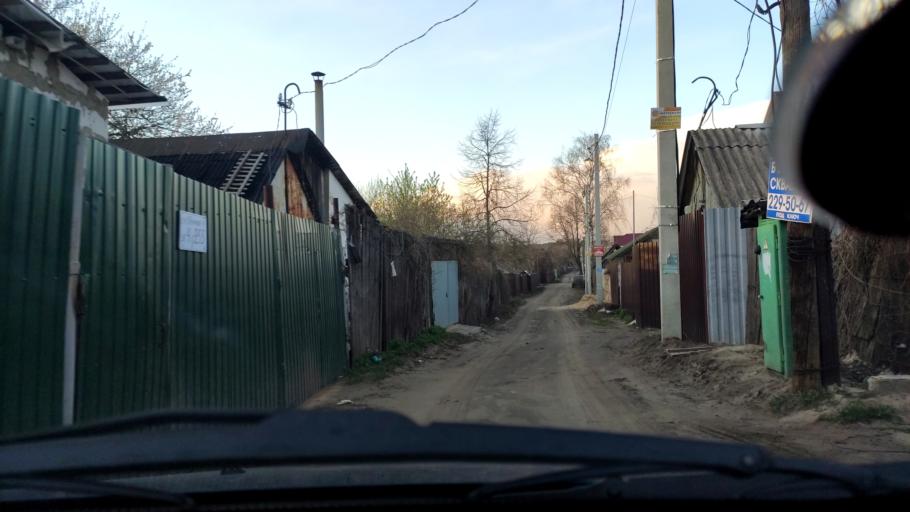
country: RU
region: Voronezj
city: Maslovka
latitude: 51.5978
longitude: 39.2298
